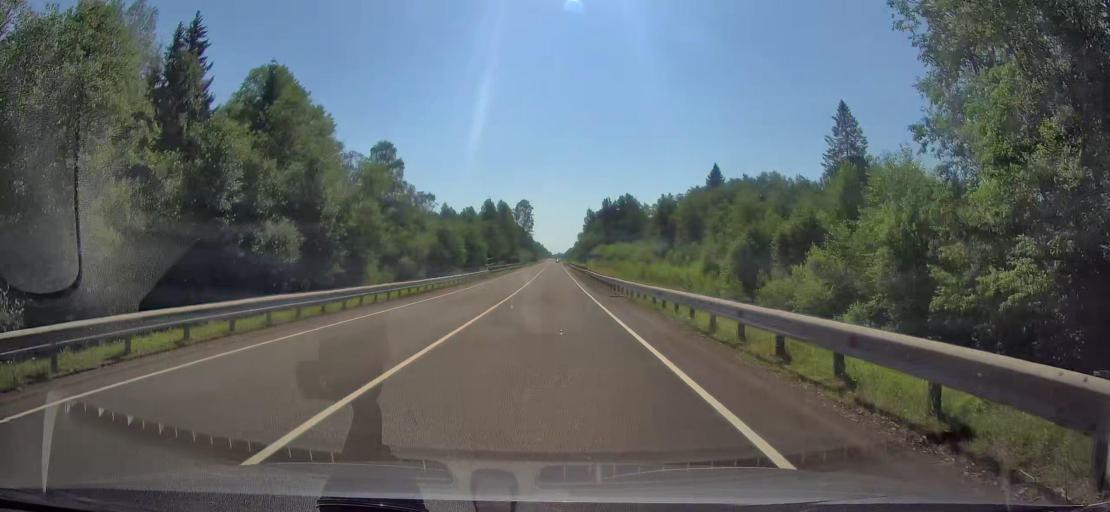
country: RU
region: Leningrad
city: Yefimovskiy
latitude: 59.4002
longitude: 34.7300
